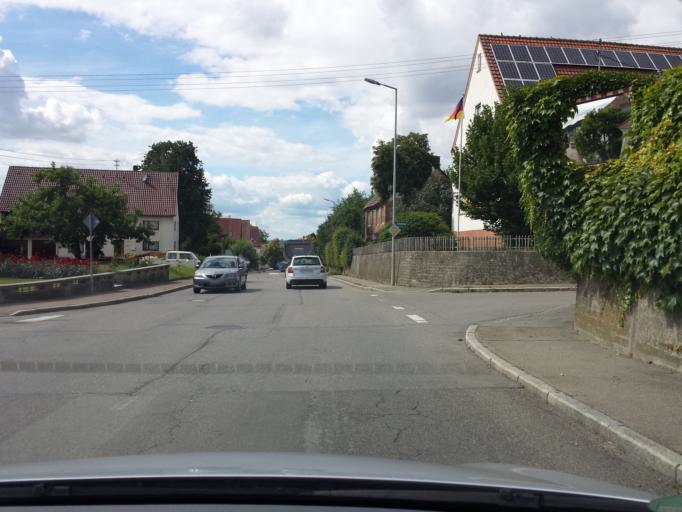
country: DE
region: Baden-Wuerttemberg
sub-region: Tuebingen Region
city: Burgrieden
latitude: 48.2236
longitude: 9.9539
